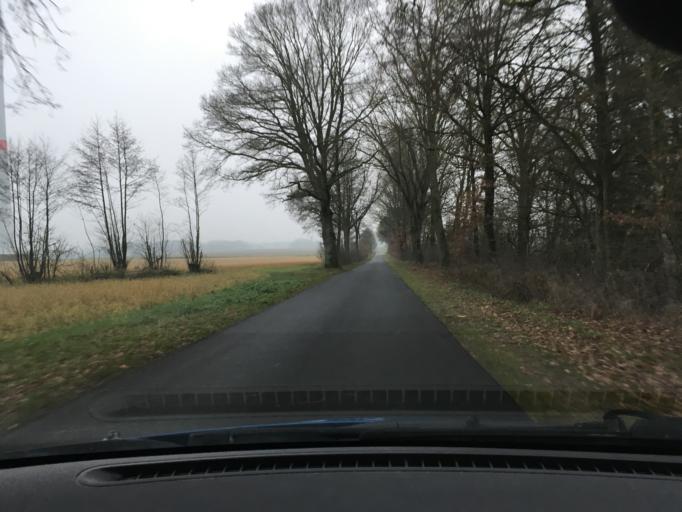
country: DE
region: Lower Saxony
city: Soderstorf
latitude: 53.0988
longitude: 10.1646
